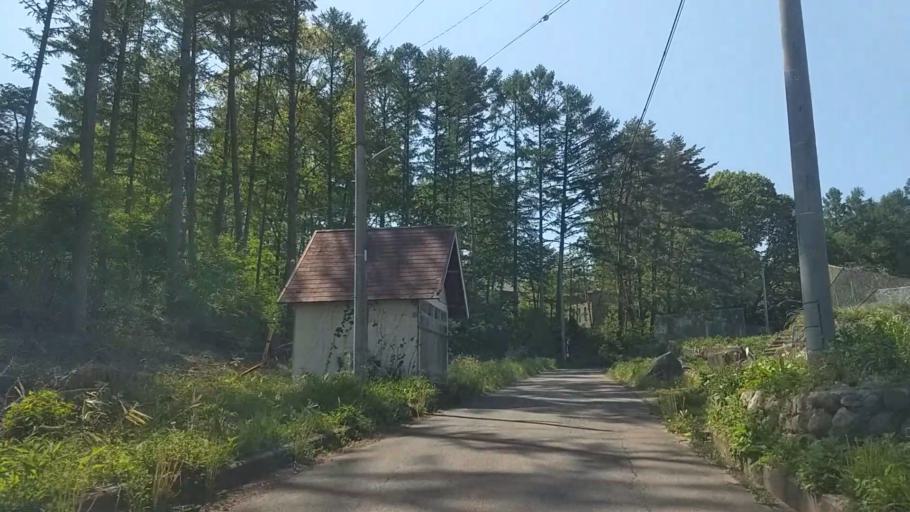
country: JP
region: Yamanashi
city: Nirasaki
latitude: 35.8885
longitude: 138.4385
